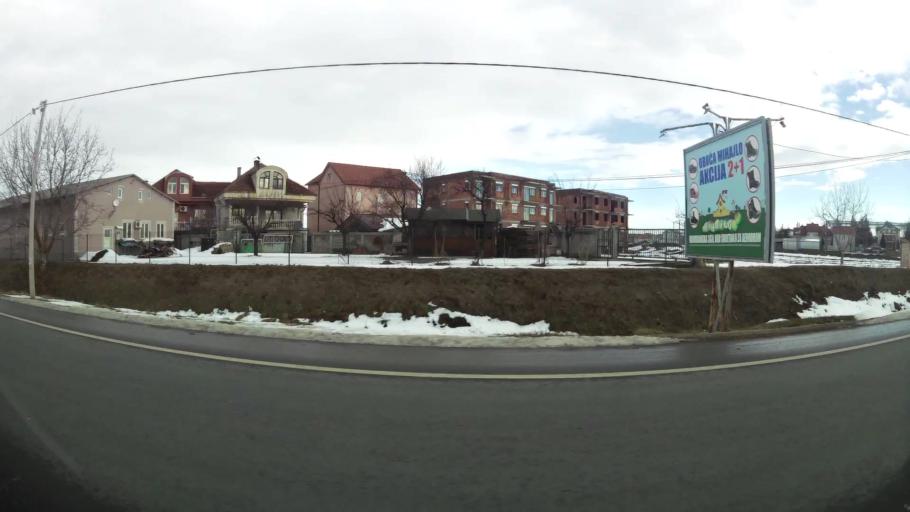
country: RS
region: Central Serbia
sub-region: Belgrade
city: Surcin
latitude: 44.8013
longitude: 20.3177
